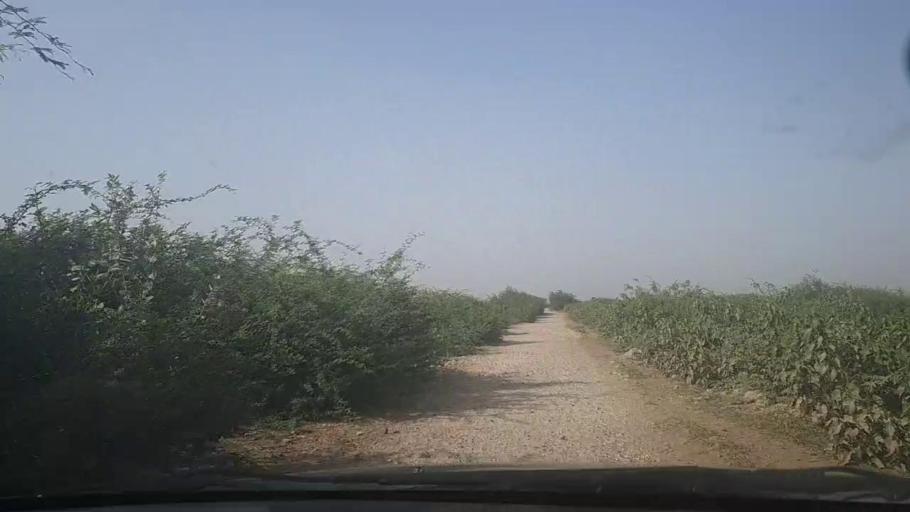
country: PK
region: Sindh
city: Keti Bandar
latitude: 24.2561
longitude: 67.5631
